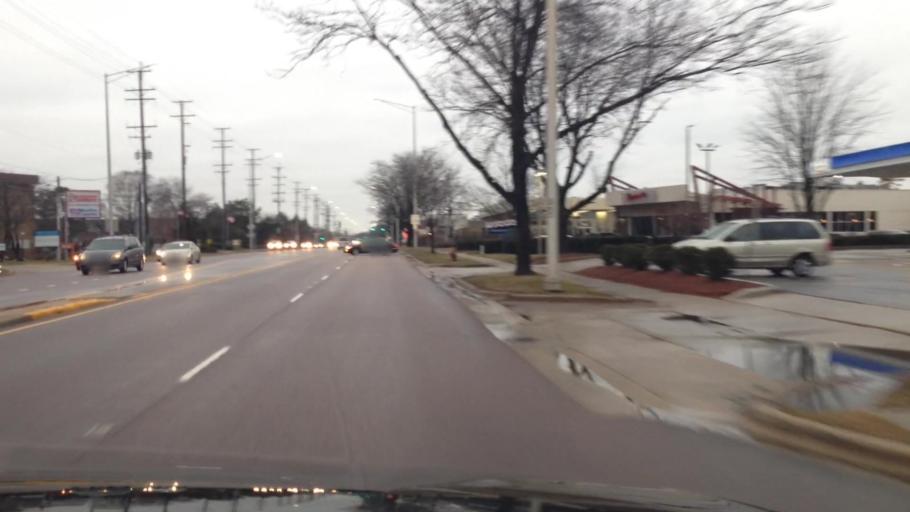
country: US
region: Illinois
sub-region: Cook County
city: Rolling Meadows
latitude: 42.0571
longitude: -88.0032
